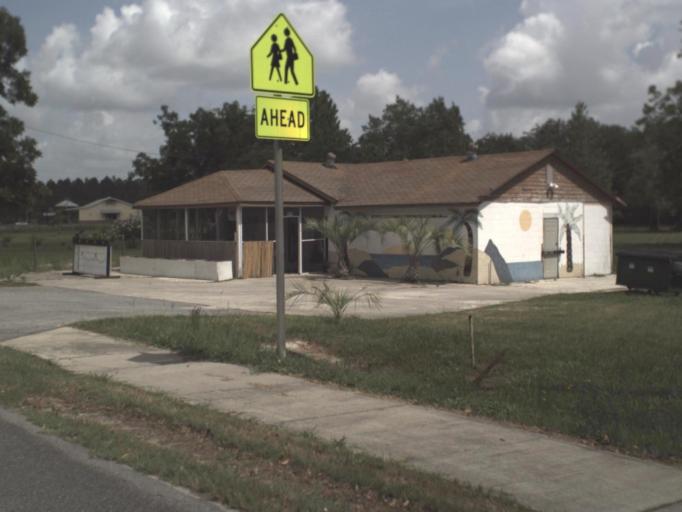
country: US
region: Florida
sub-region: Madison County
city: Madison
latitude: 30.4210
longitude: -83.3038
